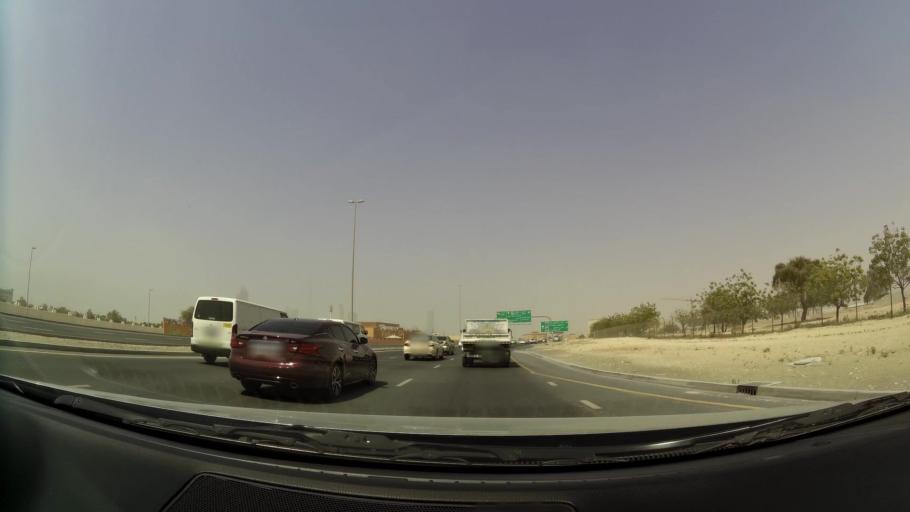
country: AE
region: Dubai
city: Dubai
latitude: 25.1628
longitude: 55.2430
